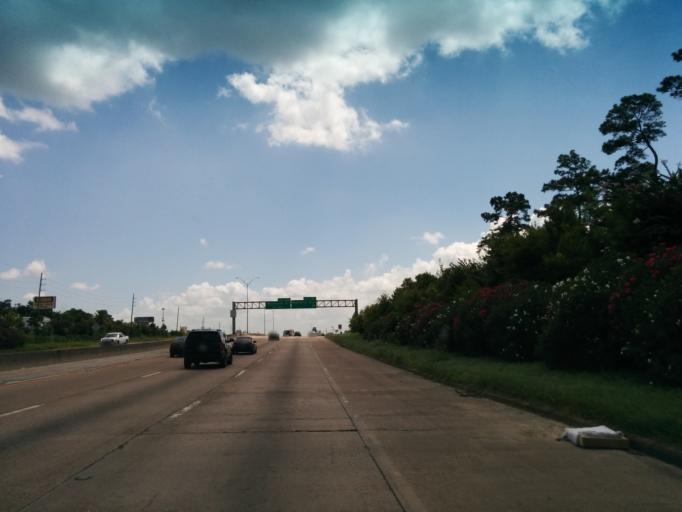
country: US
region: Texas
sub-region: Harris County
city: Channelview
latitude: 29.7861
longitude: -95.1031
